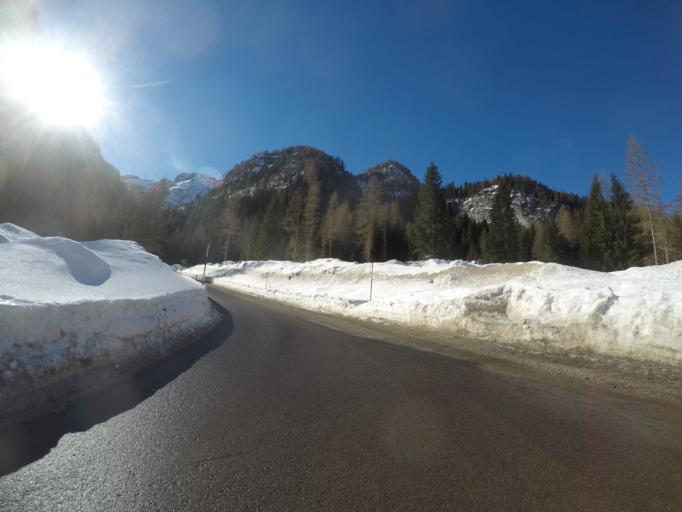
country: IT
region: Veneto
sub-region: Provincia di Belluno
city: Rocca Pietore
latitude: 46.4232
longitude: 11.9341
